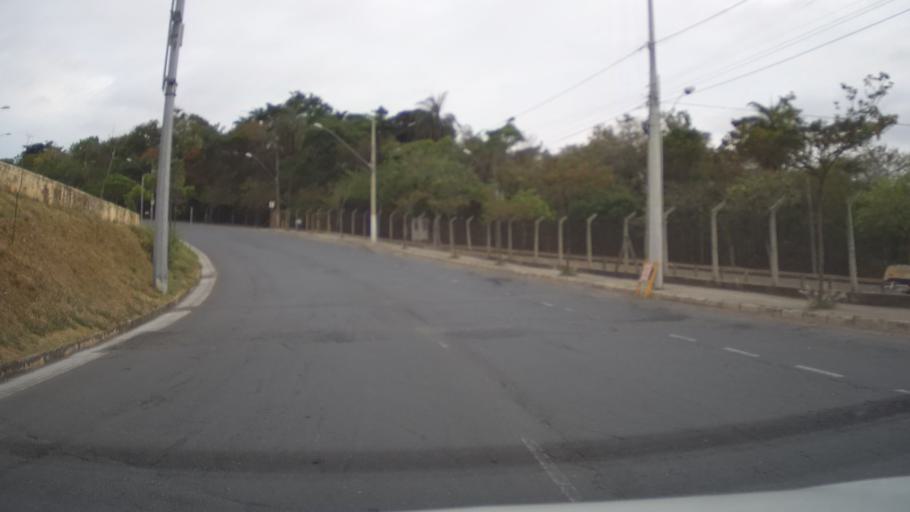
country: BR
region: Minas Gerais
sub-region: Belo Horizonte
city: Belo Horizonte
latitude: -19.8682
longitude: -43.9691
